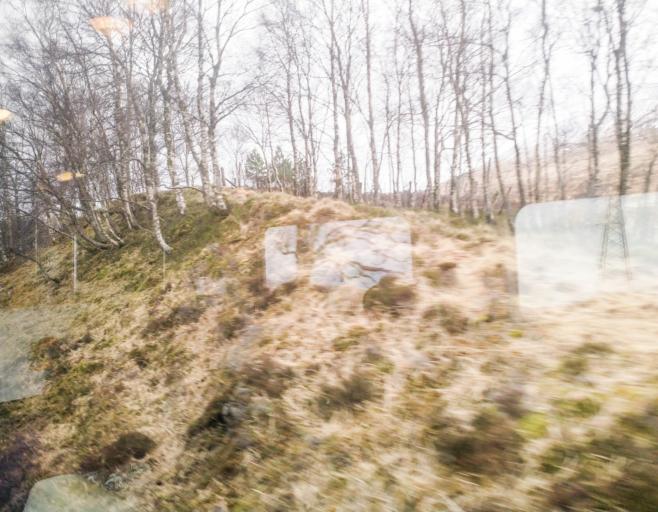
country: GB
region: Scotland
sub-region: Highland
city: Spean Bridge
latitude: 56.5827
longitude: -4.6741
